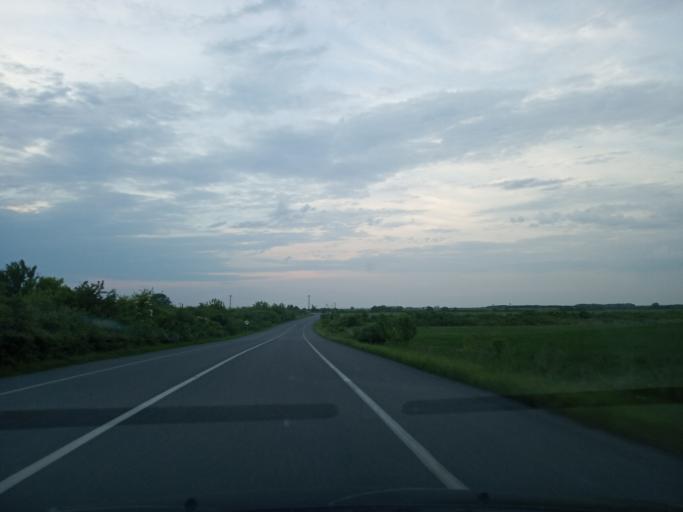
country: RO
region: Timis
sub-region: Oras Deta
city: Deta
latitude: 45.4134
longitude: 21.2297
